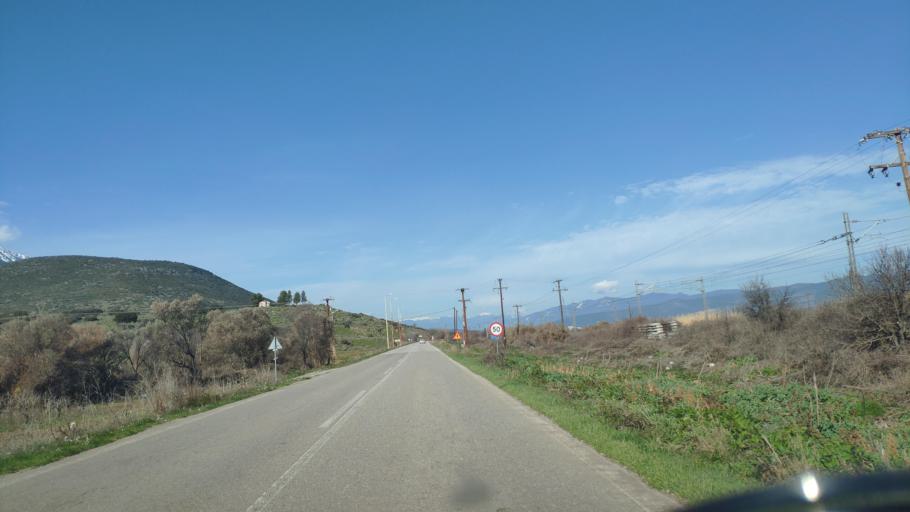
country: GR
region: Central Greece
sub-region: Nomos Fthiotidos
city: Elateia
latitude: 38.5732
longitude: 22.7639
